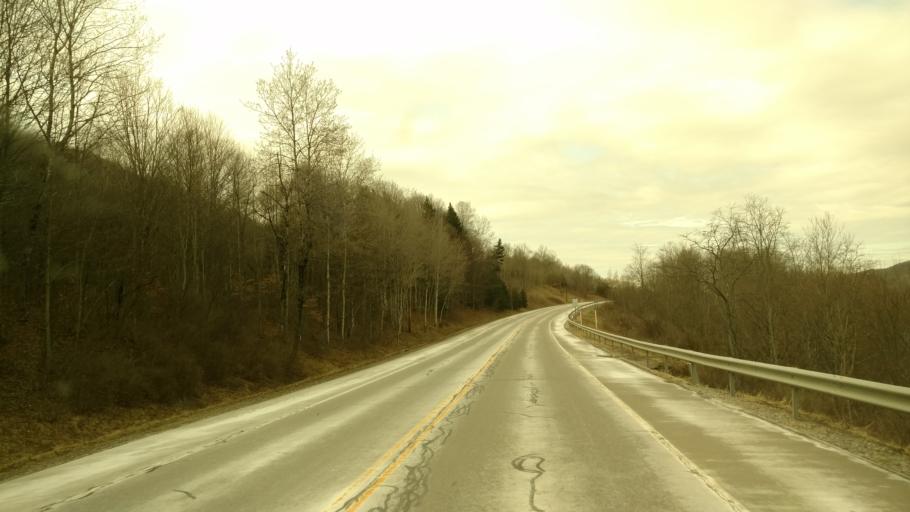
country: US
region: New York
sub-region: Allegany County
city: Wellsville
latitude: 41.9997
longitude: -77.8824
